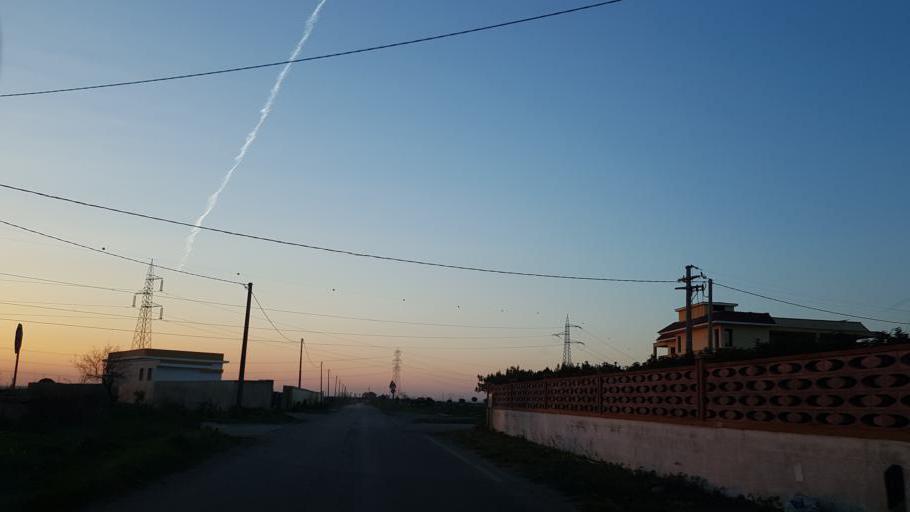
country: IT
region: Apulia
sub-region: Provincia di Brindisi
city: La Rosa
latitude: 40.5930
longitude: 17.9108
